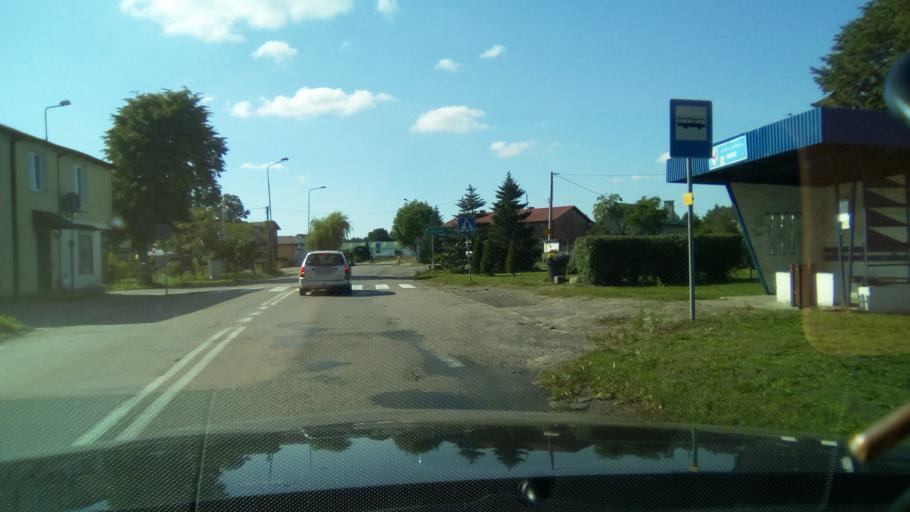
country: PL
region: West Pomeranian Voivodeship
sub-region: Powiat swidwinski
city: Rabino
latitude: 53.7751
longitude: 15.9682
